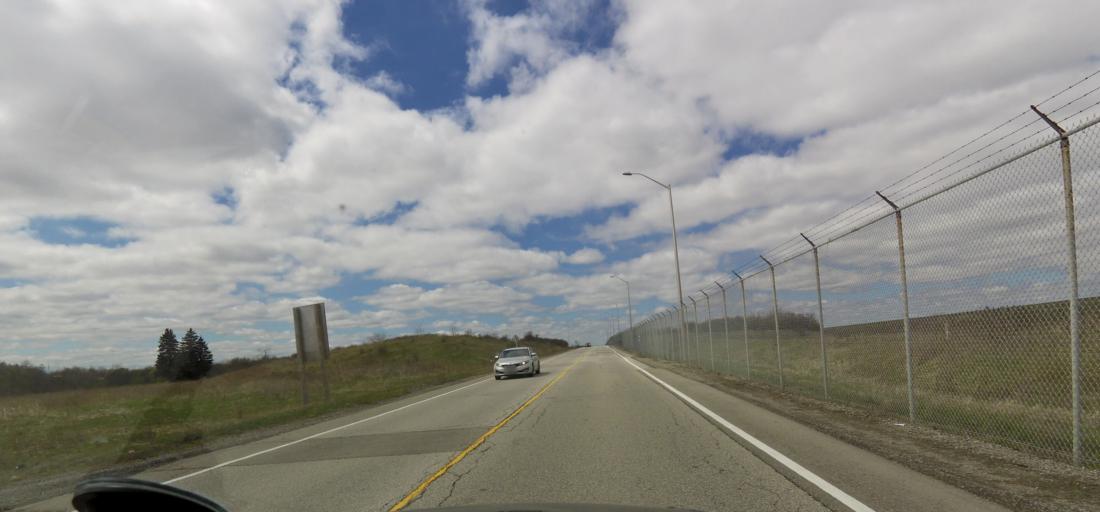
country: CA
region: Ontario
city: Etobicoke
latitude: 43.6724
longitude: -79.6400
